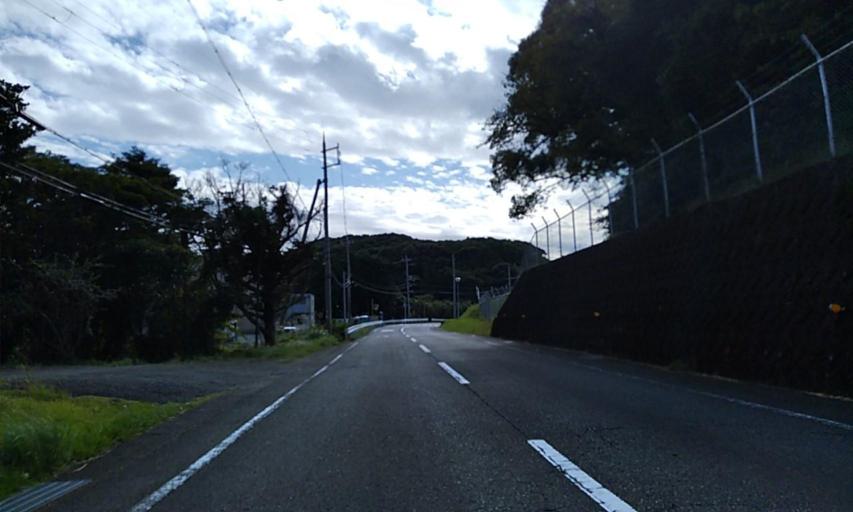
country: JP
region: Wakayama
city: Shingu
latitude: 33.4677
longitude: 135.8305
